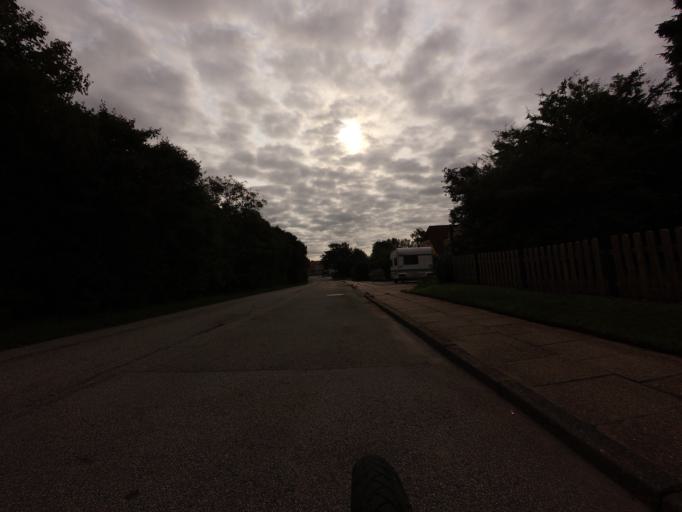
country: DK
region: North Denmark
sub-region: Hjorring Kommune
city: Hirtshals
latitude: 57.5631
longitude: 10.0272
